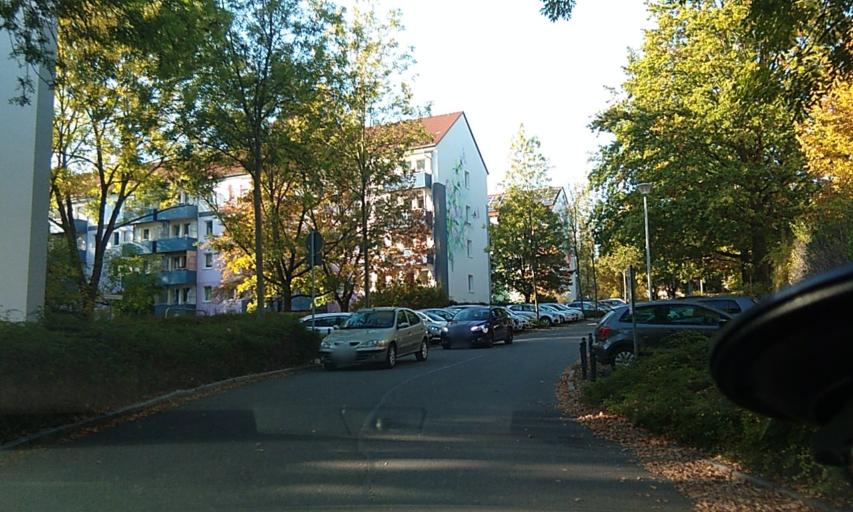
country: DE
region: Saxony
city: Wittgensdorf
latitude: 50.8404
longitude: 12.8779
